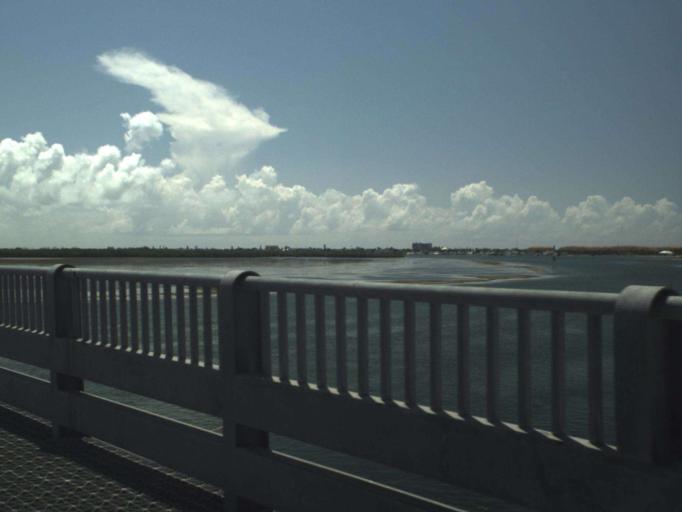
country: US
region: Florida
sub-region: Saint Lucie County
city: Fort Pierce
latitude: 27.4719
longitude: -80.3246
